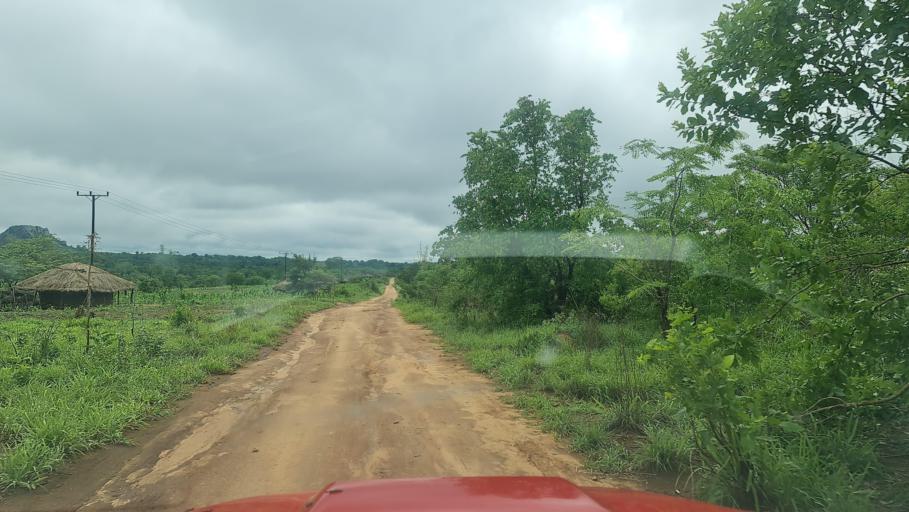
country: MW
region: Southern Region
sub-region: Nsanje District
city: Nsanje
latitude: -17.1919
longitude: 35.8635
